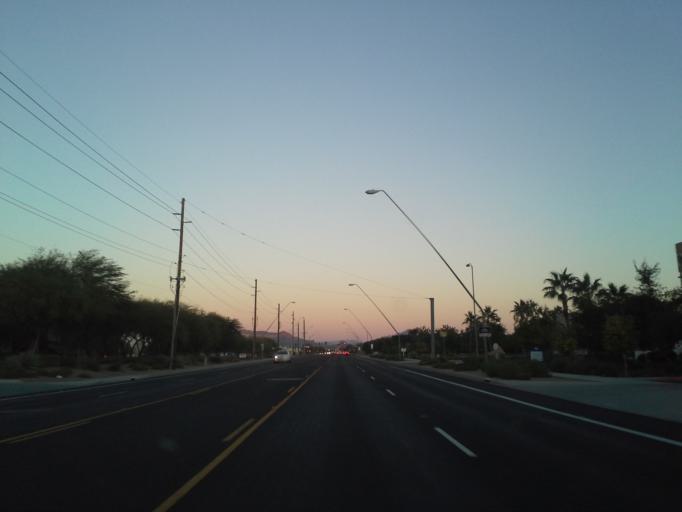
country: US
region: Arizona
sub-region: Maricopa County
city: Mesa
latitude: 33.4664
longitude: -111.7404
